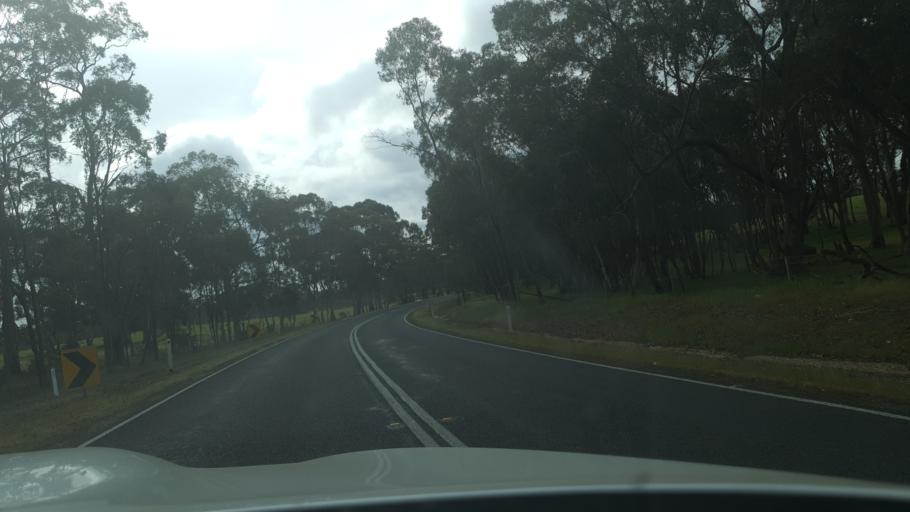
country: AU
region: Victoria
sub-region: Central Goldfields
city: Maryborough
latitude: -37.2028
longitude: 143.7076
